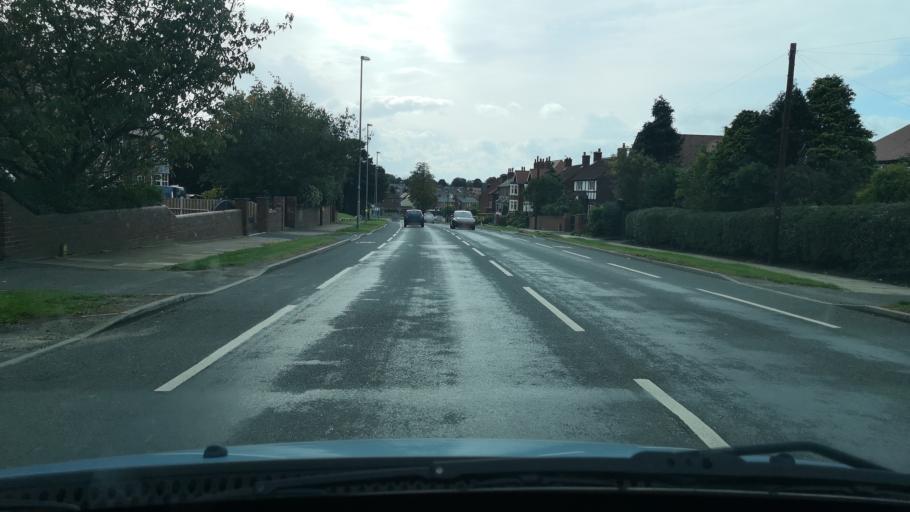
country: GB
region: England
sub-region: City and Borough of Wakefield
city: Featherstone
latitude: 53.6763
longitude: -1.3417
